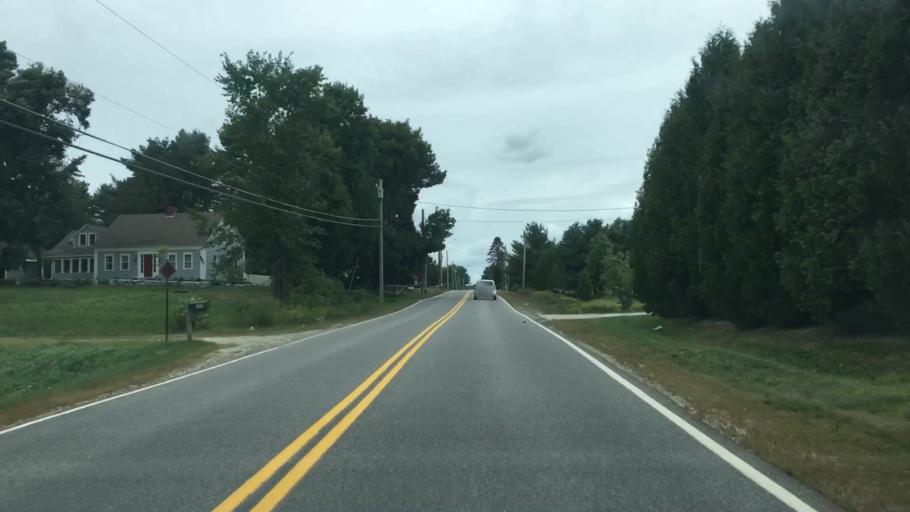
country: US
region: Maine
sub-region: Cumberland County
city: Yarmouth
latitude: 43.8650
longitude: -70.2249
